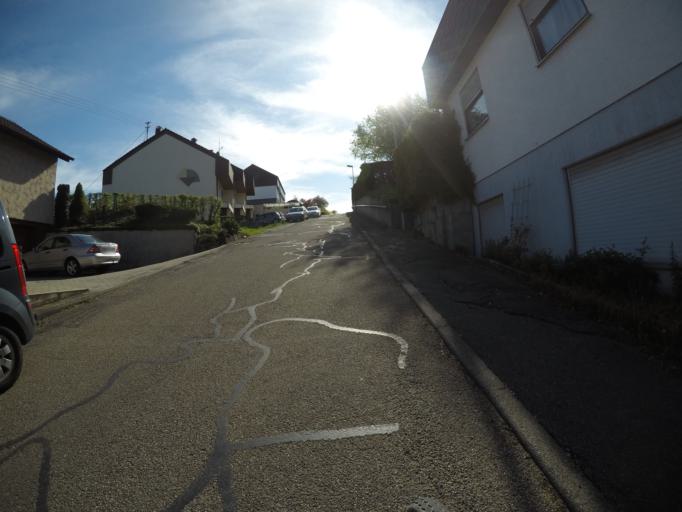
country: DE
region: Baden-Wuerttemberg
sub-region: Regierungsbezirk Stuttgart
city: Neckartailfingen
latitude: 48.6108
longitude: 9.2592
